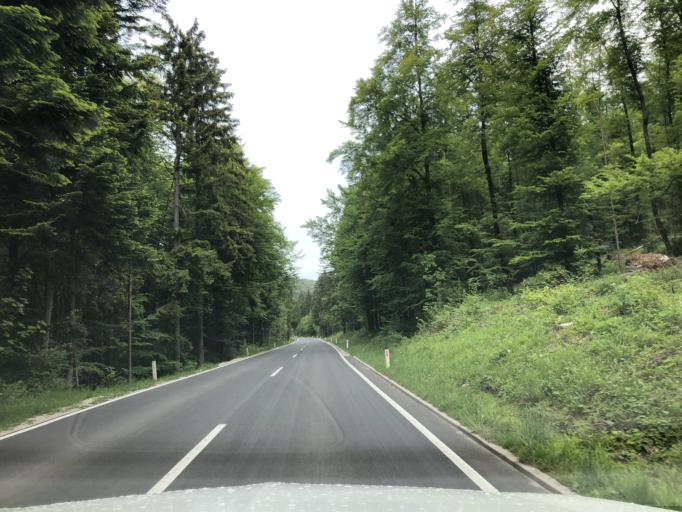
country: SI
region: Bloke
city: Nova Vas
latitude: 45.7540
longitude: 14.4671
